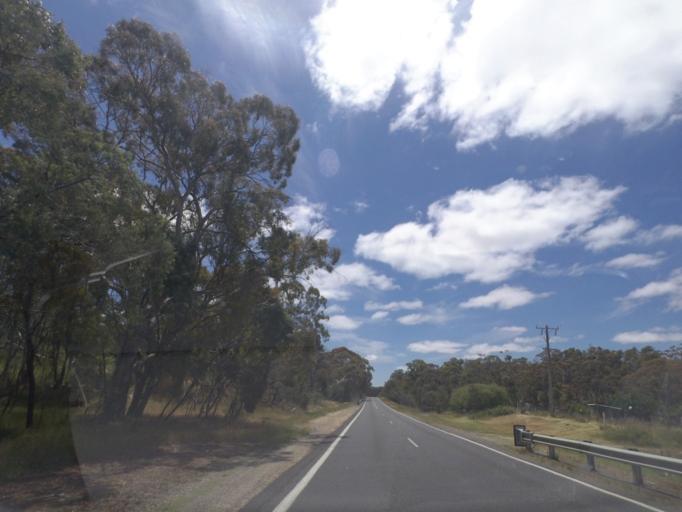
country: AU
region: Victoria
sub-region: Mount Alexander
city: Castlemaine
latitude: -37.2949
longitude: 144.1628
